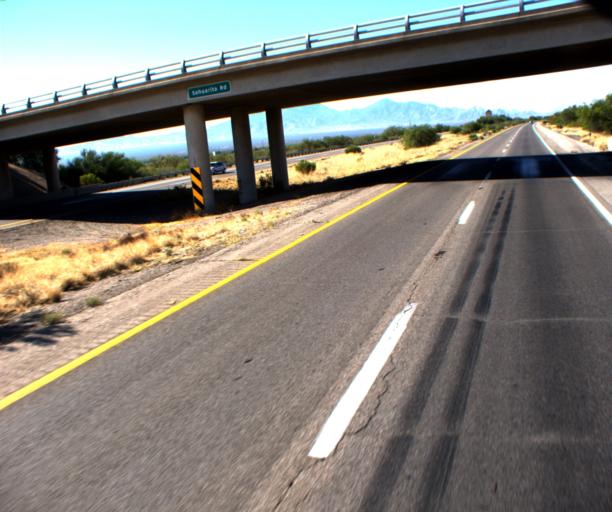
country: US
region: Arizona
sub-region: Pima County
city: Sahuarita
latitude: 31.9582
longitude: -110.9879
